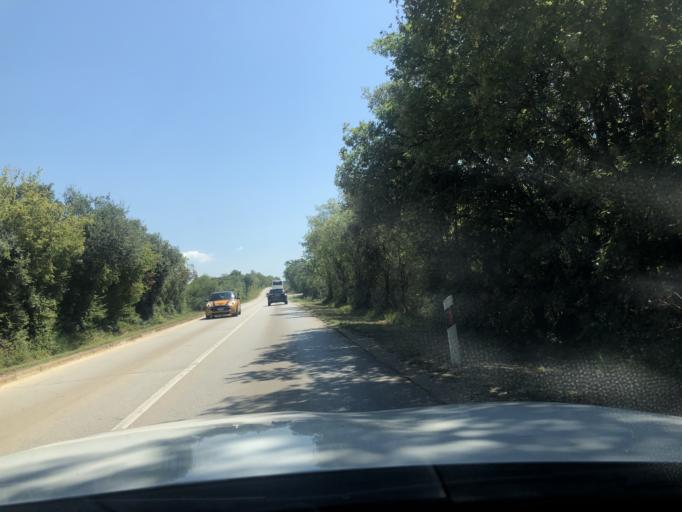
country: HR
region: Istarska
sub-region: Grad Rovinj
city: Rovinj
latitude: 45.0551
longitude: 13.7107
